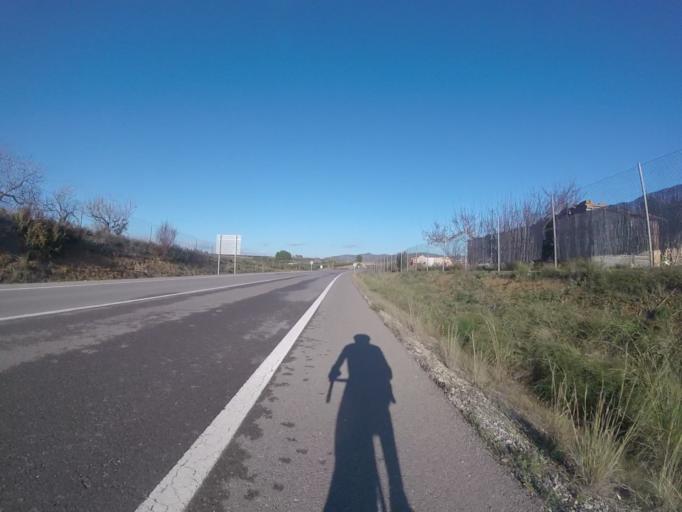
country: ES
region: Valencia
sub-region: Provincia de Castello
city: Cuevas de Vinroma
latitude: 40.3087
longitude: 0.1148
